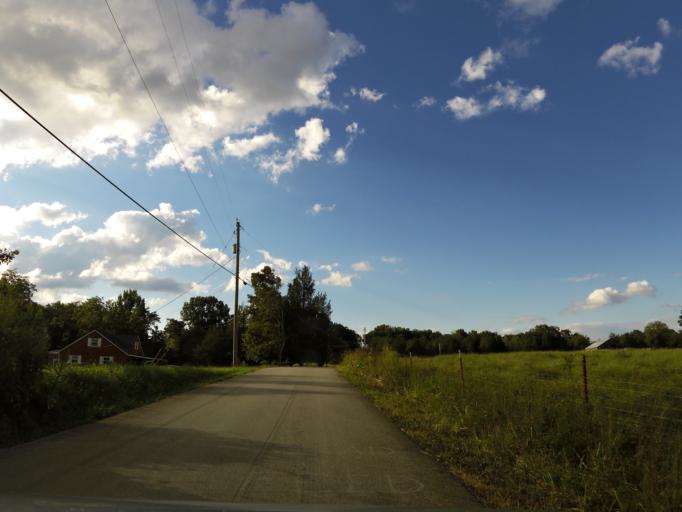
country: US
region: Tennessee
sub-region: Union County
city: Condon
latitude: 36.1280
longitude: -83.7784
